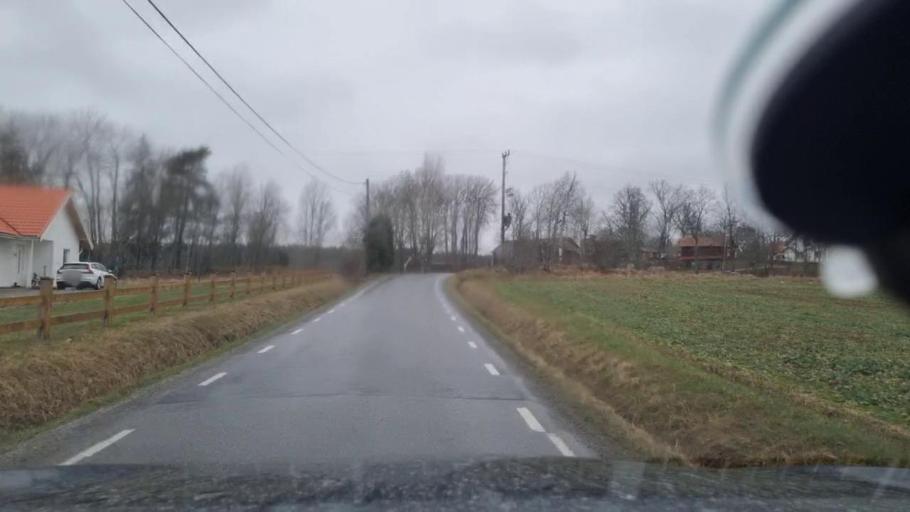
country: SE
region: Stockholm
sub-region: Vallentuna Kommun
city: Vallentuna
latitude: 59.5245
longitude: 18.0402
